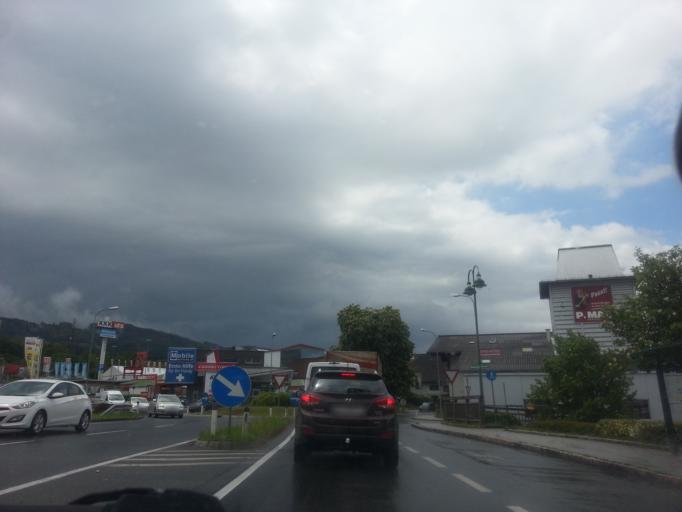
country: AT
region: Salzburg
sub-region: Politischer Bezirk Salzburg-Umgebung
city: Eugendorf
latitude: 47.8593
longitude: 13.1258
